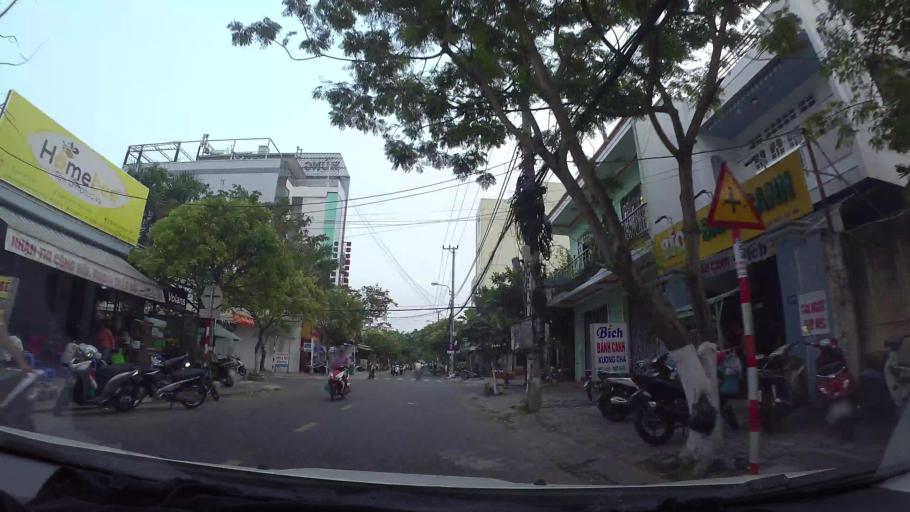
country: VN
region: Da Nang
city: Son Tra
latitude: 16.0479
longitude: 108.2413
